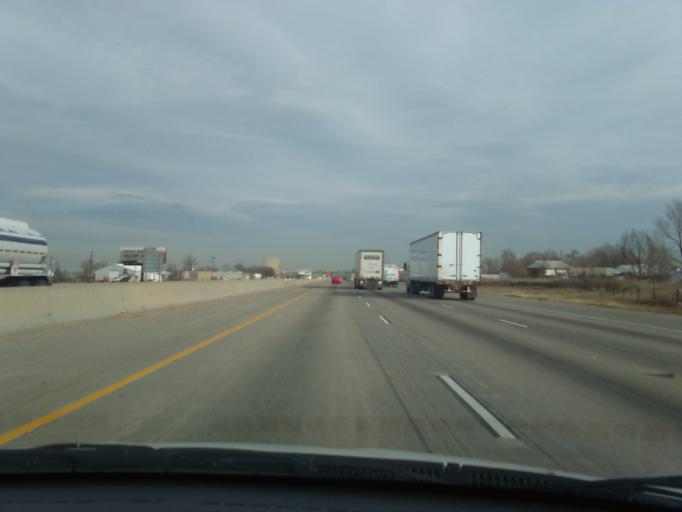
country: US
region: Colorado
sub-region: Adams County
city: Derby
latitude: 39.8522
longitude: -104.9180
